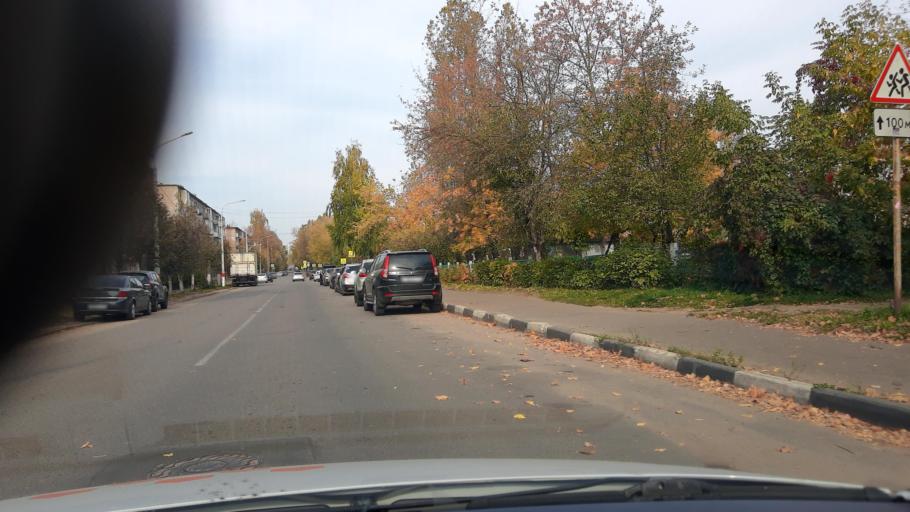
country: RU
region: Moskovskaya
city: Elektrostal'
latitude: 55.7983
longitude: 38.4353
